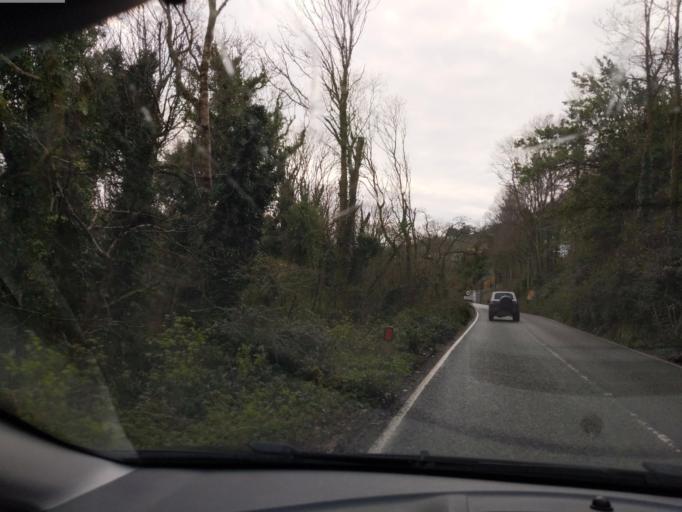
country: GB
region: England
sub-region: Cornwall
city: Looe
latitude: 50.3708
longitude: -4.3879
